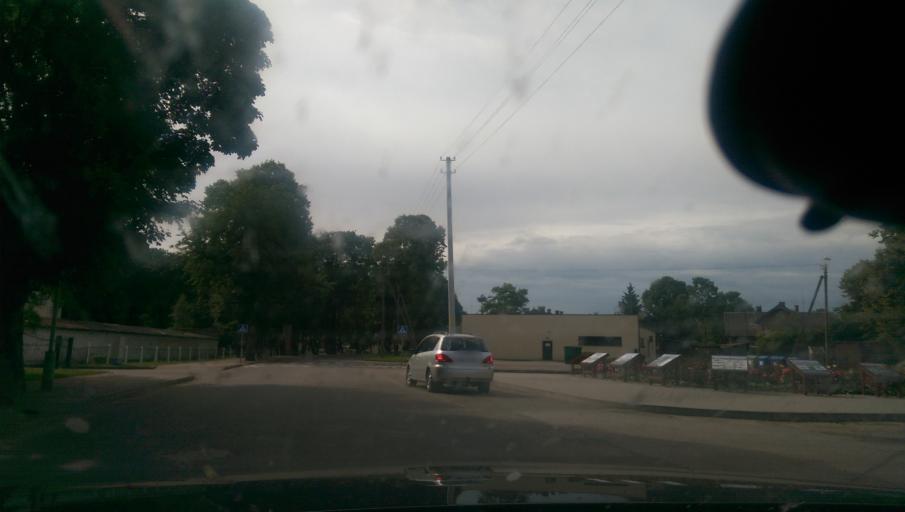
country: LT
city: Rusne
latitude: 55.2988
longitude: 21.3739
